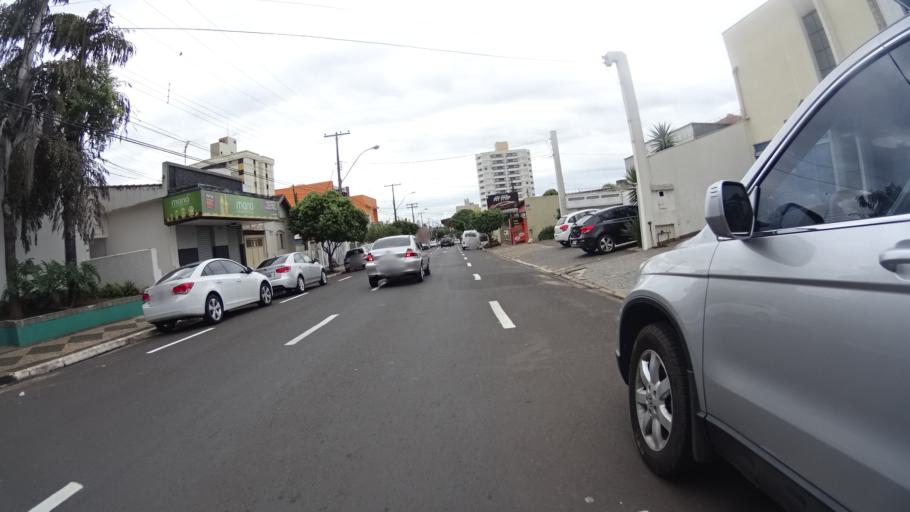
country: BR
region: Sao Paulo
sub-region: Marilia
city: Marilia
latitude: -22.2195
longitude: -49.9413
